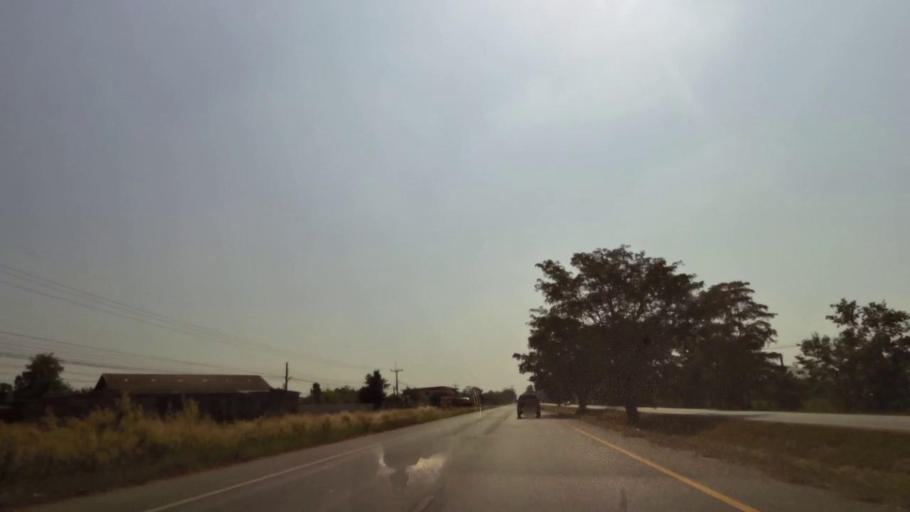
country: TH
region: Phichit
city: Bueng Na Rang
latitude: 16.3354
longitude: 100.1284
